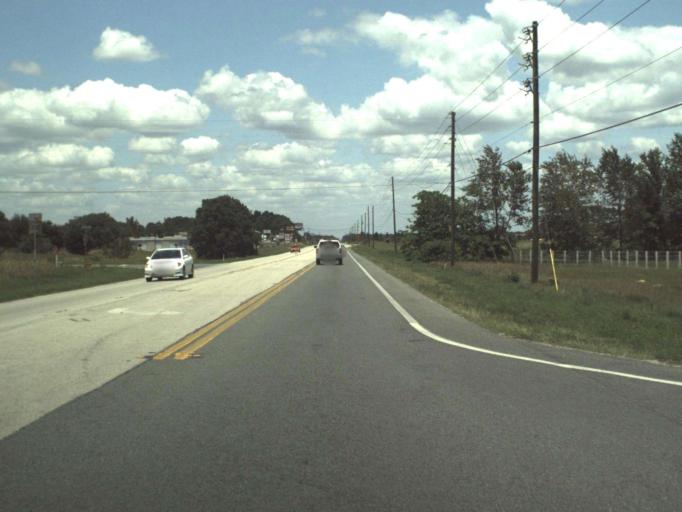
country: US
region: Florida
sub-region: Marion County
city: Silver Springs Shores
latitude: 29.0979
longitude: -82.0535
